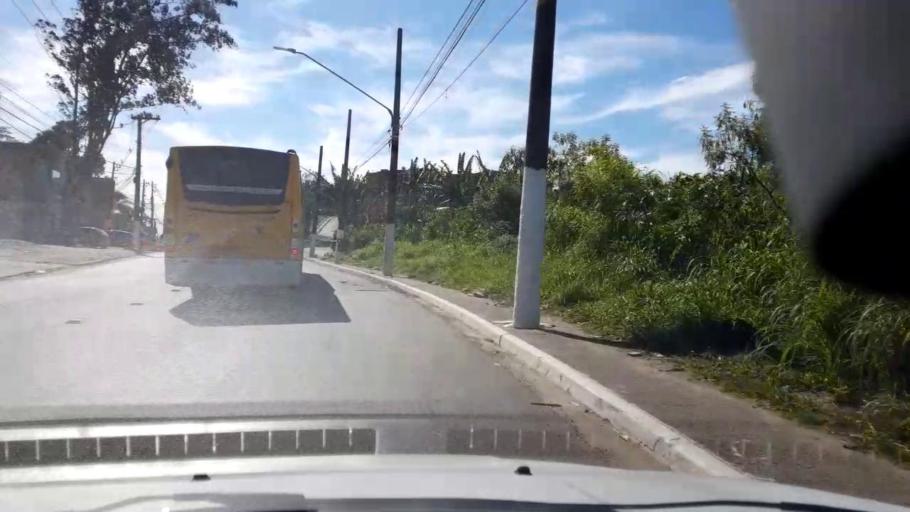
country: BR
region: Sao Paulo
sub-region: Ferraz De Vasconcelos
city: Ferraz de Vasconcelos
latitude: -23.5887
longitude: -46.4152
